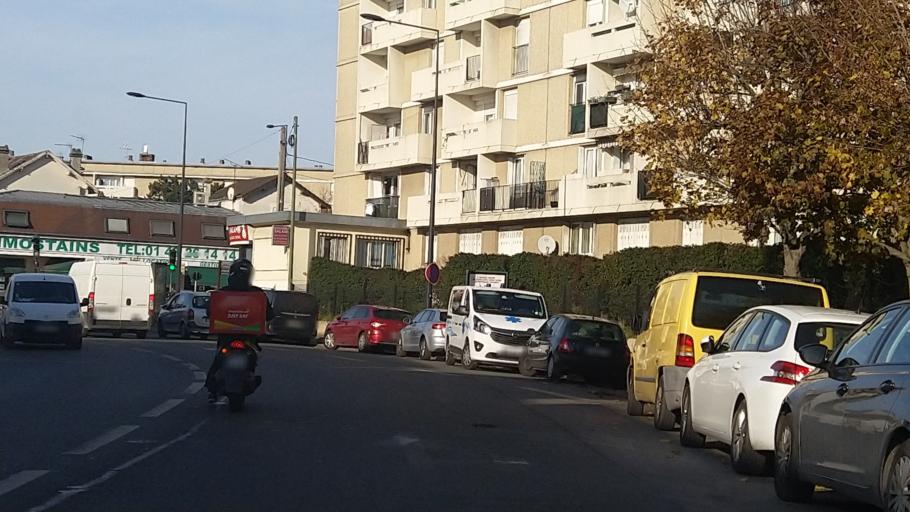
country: FR
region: Ile-de-France
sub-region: Departement de Seine-Saint-Denis
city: Stains
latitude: 48.9604
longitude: 2.3820
